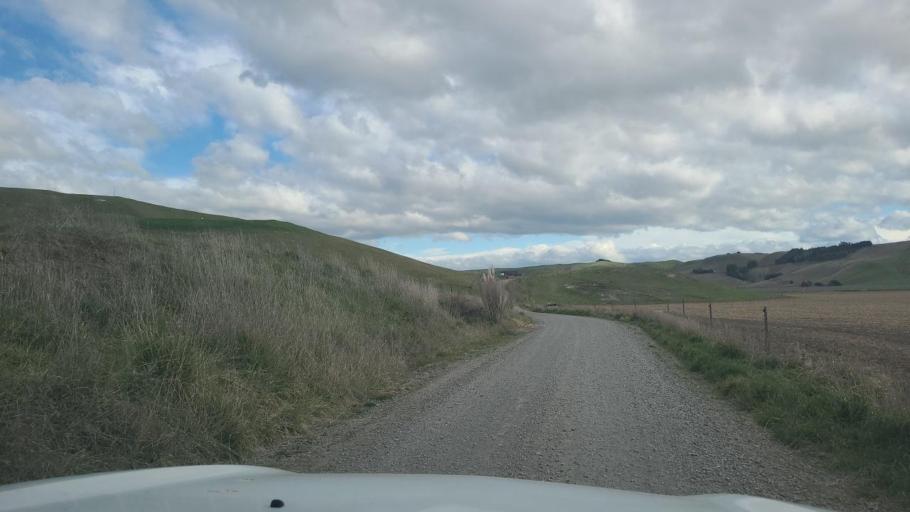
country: NZ
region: Hawke's Bay
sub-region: Hastings District
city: Hastings
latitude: -39.6626
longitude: 176.6654
